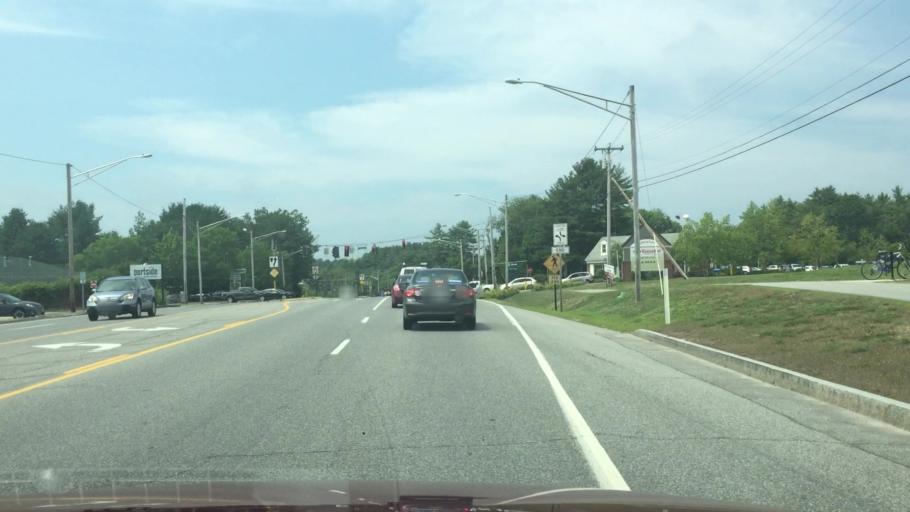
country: US
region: Maine
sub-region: Cumberland County
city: Yarmouth
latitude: 43.8042
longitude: -70.1780
